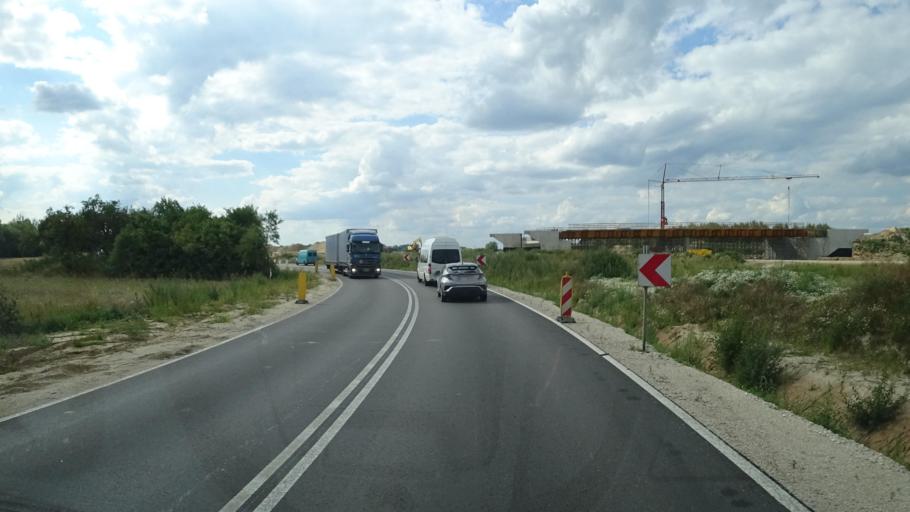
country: PL
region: Masovian Voivodeship
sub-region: Powiat ostrowski
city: Ostrow Mazowiecka
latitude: 52.8193
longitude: 21.9147
